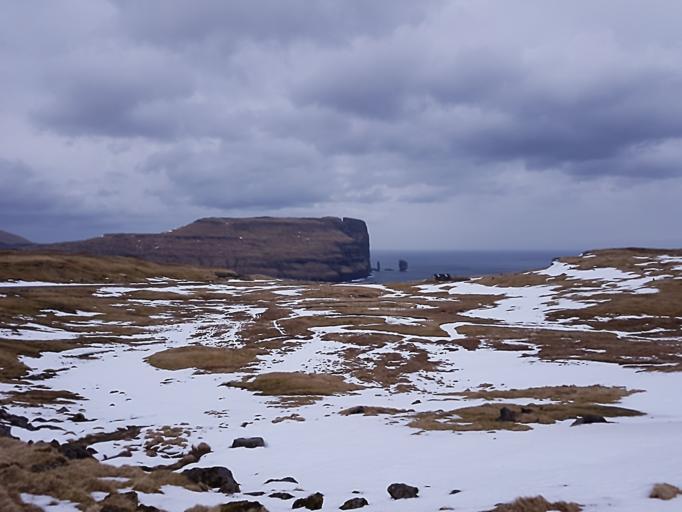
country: FO
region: Eysturoy
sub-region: Eidi
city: Eidi
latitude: 62.3024
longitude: -7.0518
